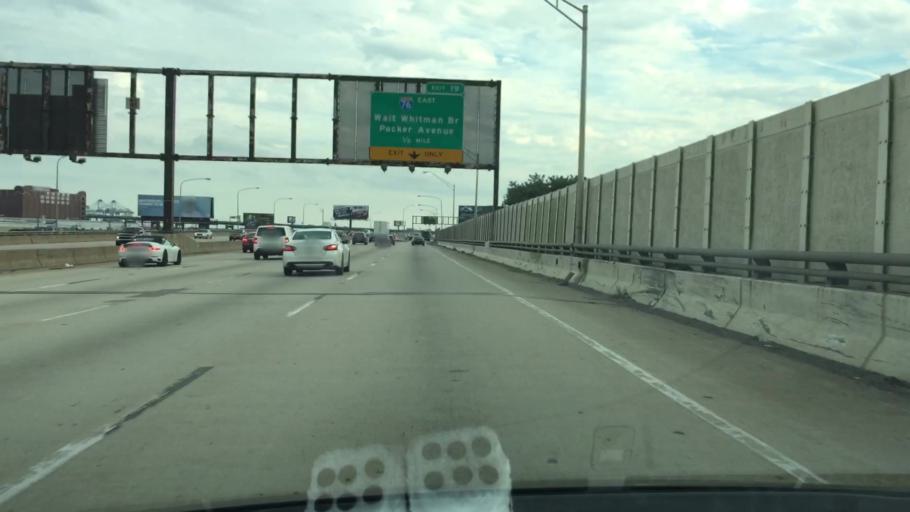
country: US
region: New Jersey
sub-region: Camden County
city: Camden
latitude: 39.9194
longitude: -75.1482
